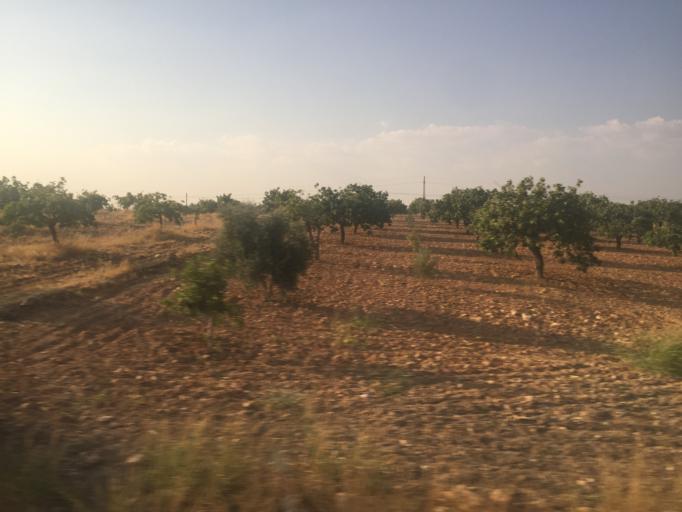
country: TR
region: Sanliurfa
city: Birecik
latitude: 37.0167
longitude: 37.8885
